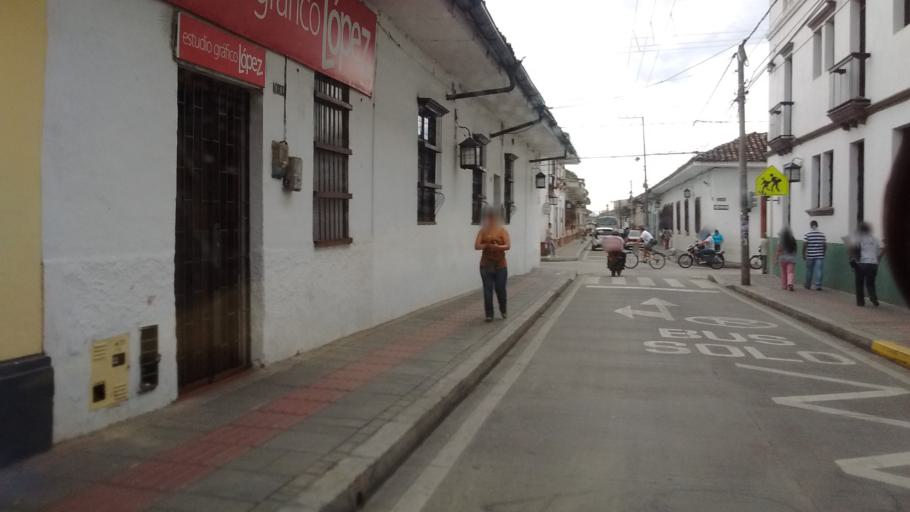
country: CO
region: Cauca
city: Popayan
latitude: 2.4390
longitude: -76.6075
